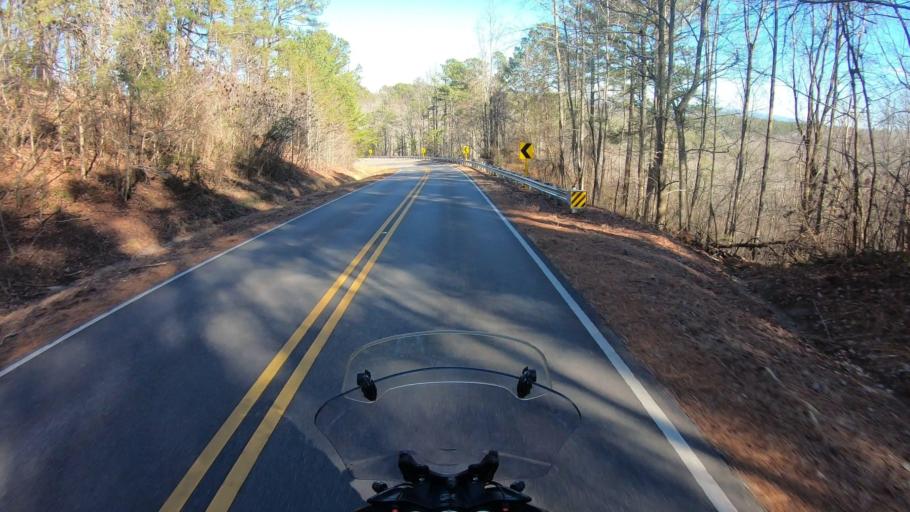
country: US
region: Alabama
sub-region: Calhoun County
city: Oxford
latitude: 33.5227
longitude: -85.7498
